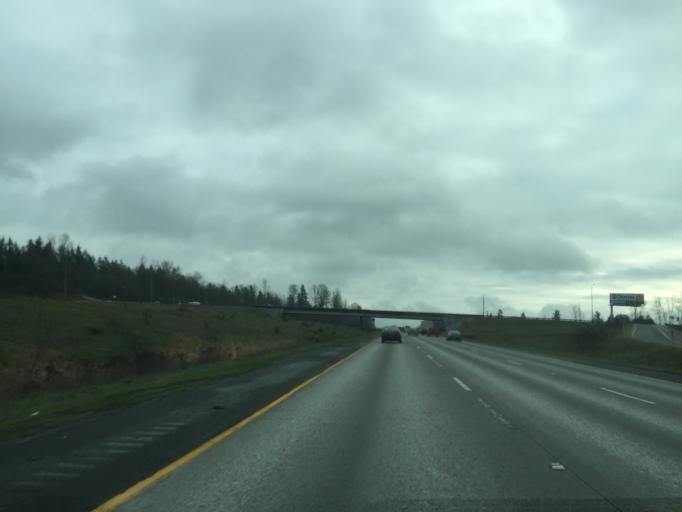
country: US
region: Washington
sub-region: Snohomish County
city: Bryant
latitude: 48.2123
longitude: -122.2174
